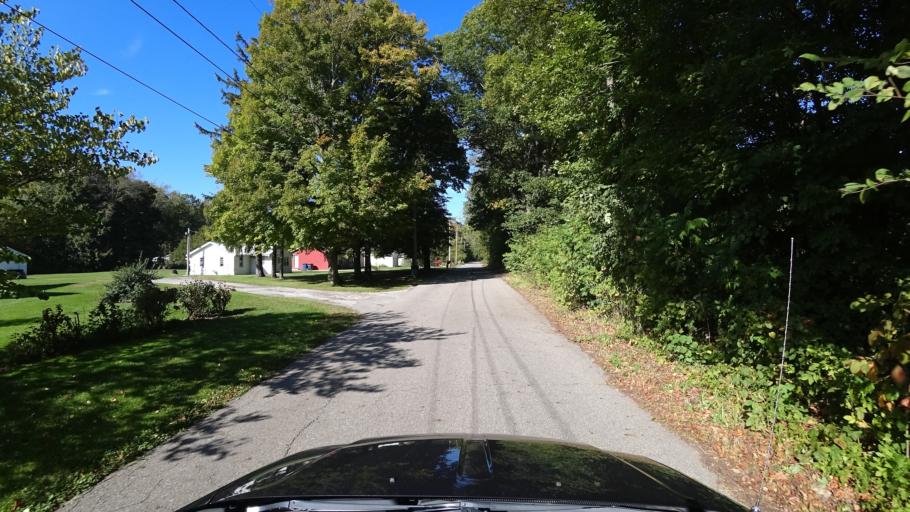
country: US
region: Indiana
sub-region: LaPorte County
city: Trail Creek
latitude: 41.7010
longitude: -86.8357
